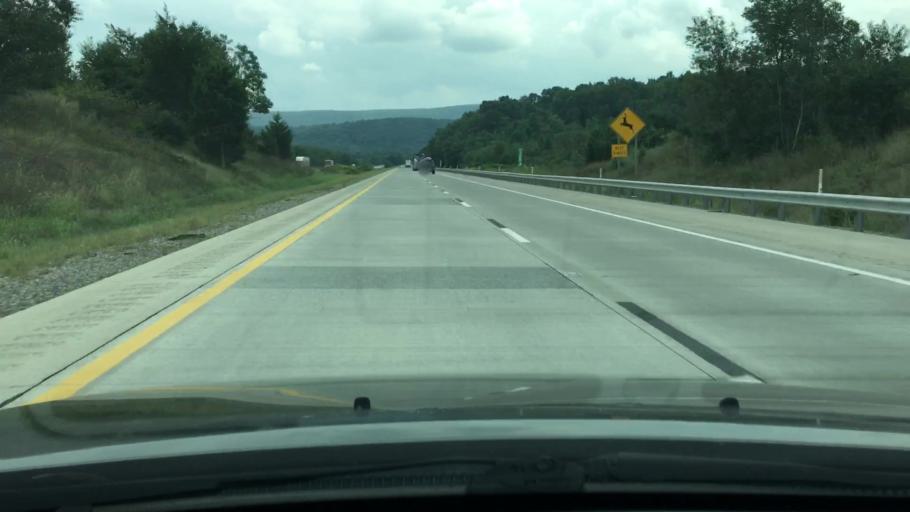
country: US
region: Pennsylvania
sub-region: Schuylkill County
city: Pine Grove
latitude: 40.5458
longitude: -76.4303
